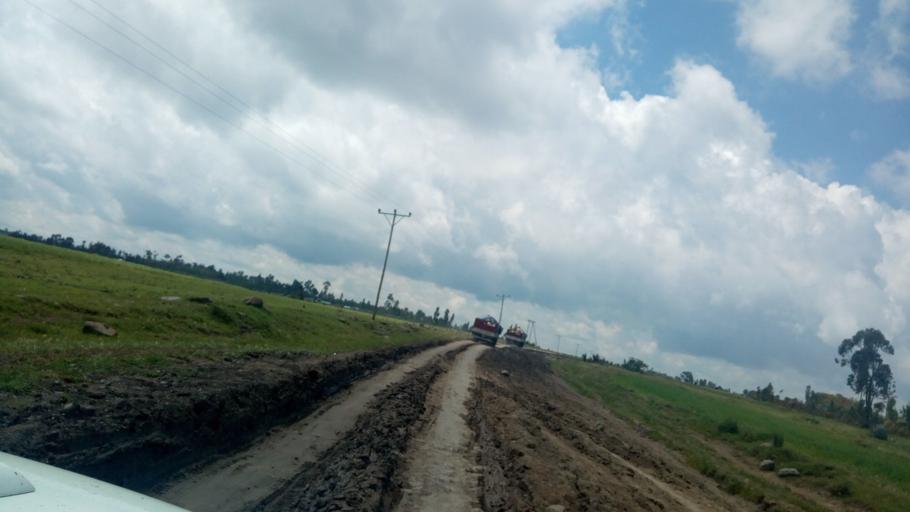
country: ET
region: Oromiya
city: Sendafa
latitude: 8.9898
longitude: 39.1241
